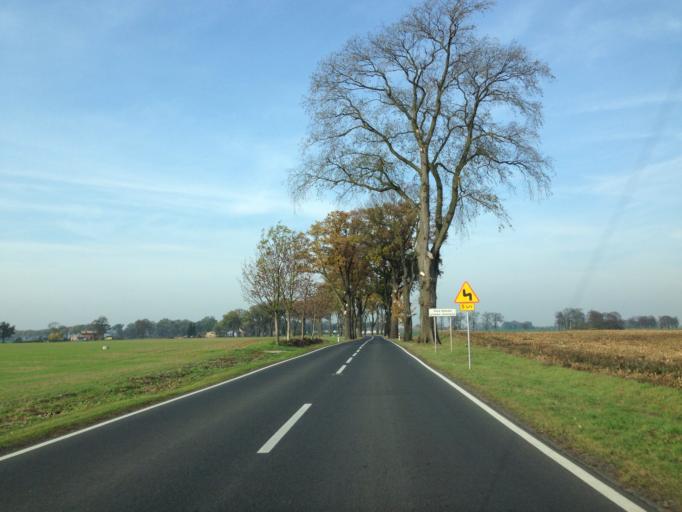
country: PL
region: Kujawsko-Pomorskie
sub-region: Powiat swiecki
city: Pruszcz
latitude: 53.2758
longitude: 18.1641
